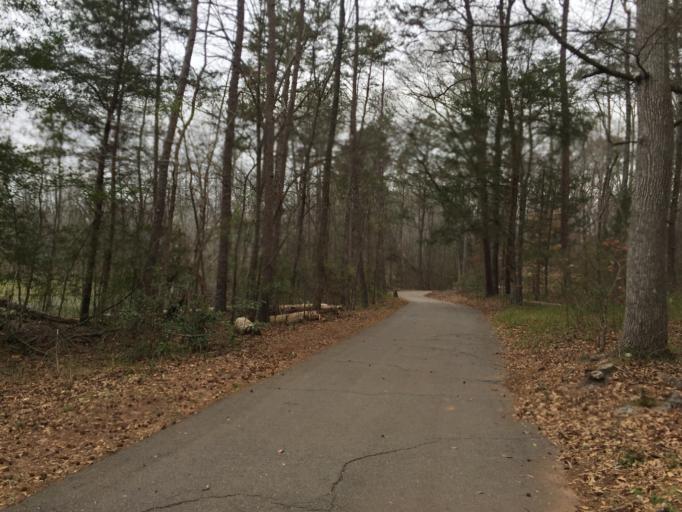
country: US
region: South Carolina
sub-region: Greenville County
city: Mauldin
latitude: 34.7755
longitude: -82.3613
